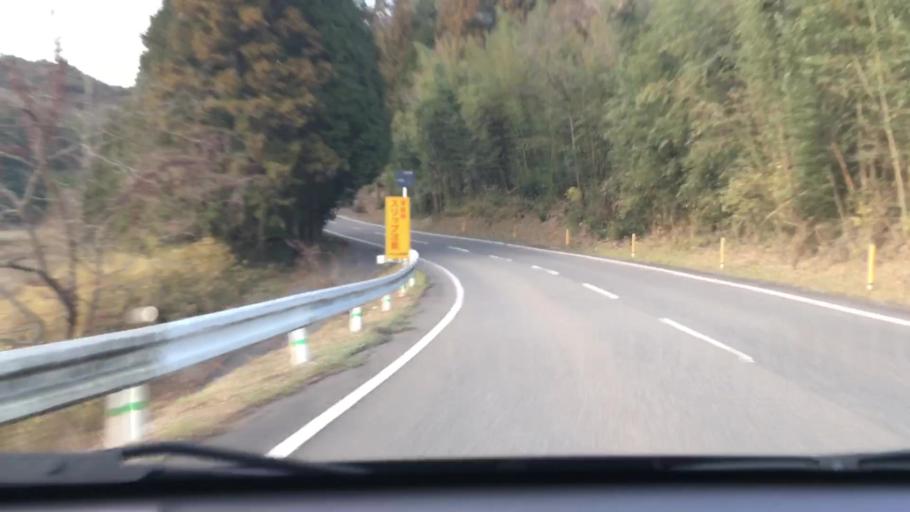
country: JP
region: Oita
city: Hiji
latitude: 33.4146
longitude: 131.4202
